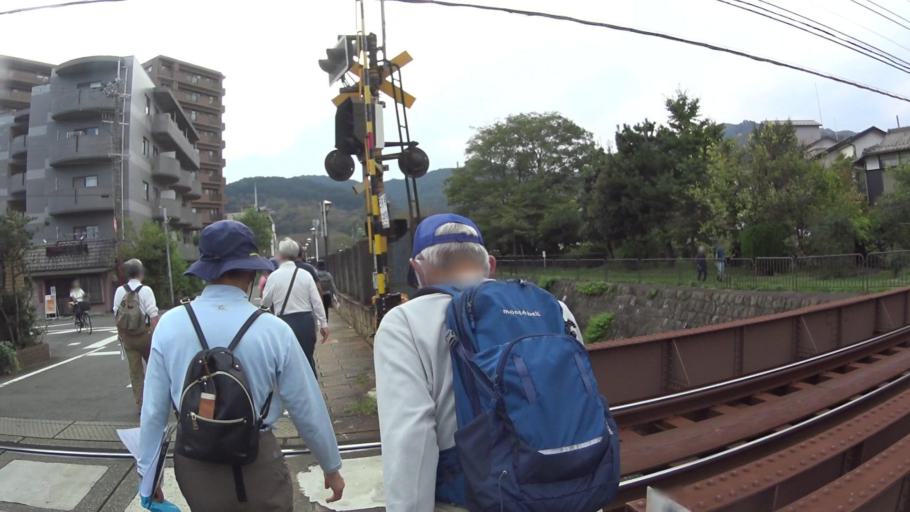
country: JP
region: Shiga Prefecture
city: Hikone
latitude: 35.2688
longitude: 136.3707
